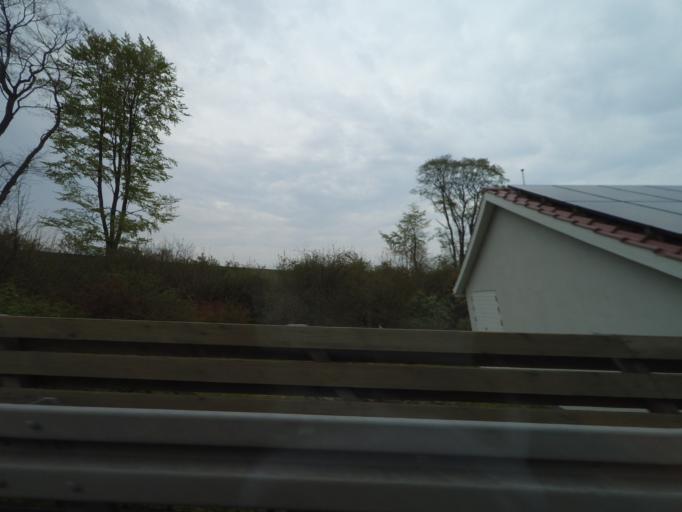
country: DK
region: South Denmark
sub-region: Svendborg Kommune
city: Svendborg
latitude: 55.1607
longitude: 10.6509
